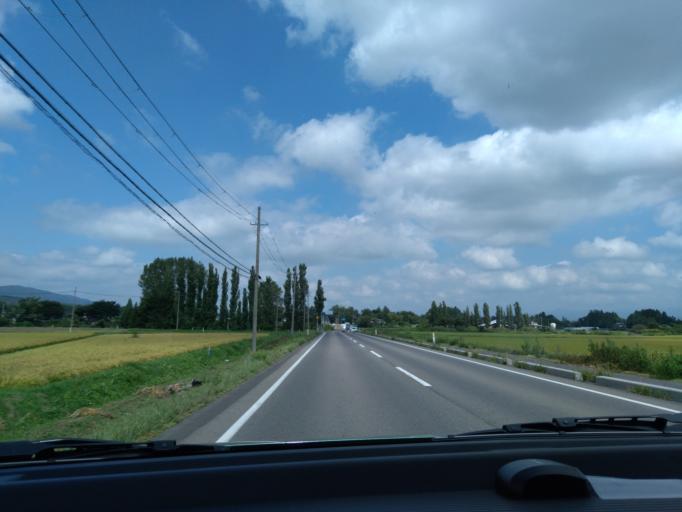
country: JP
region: Iwate
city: Hanamaki
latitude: 39.4551
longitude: 141.0991
